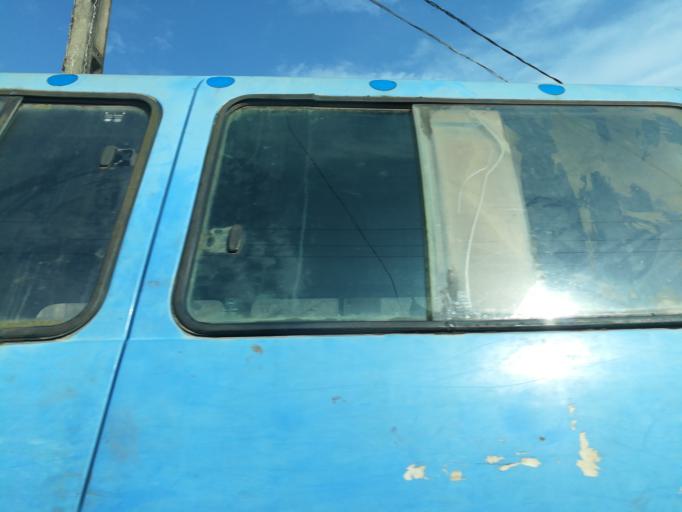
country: NG
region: Lagos
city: Ojota
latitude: 6.6018
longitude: 3.4184
